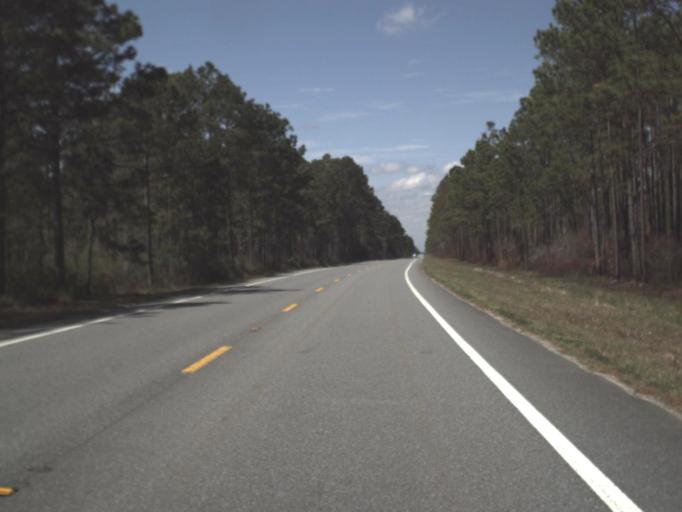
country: US
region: Florida
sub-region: Gadsden County
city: Midway
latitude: 30.3587
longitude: -84.5305
